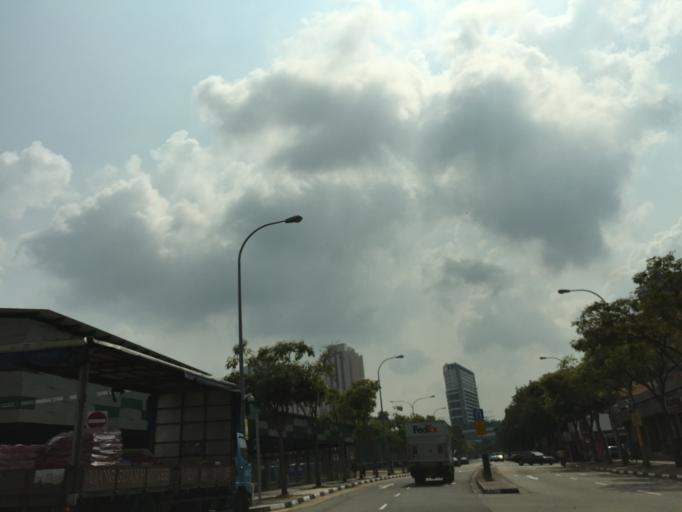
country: SG
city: Singapore
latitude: 1.3072
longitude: 103.8500
